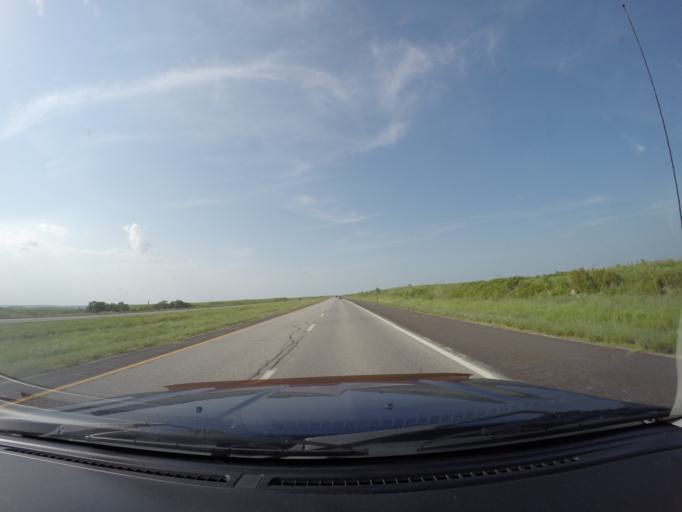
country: US
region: Kansas
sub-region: Riley County
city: Manhattan
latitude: 39.1008
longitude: -96.5381
